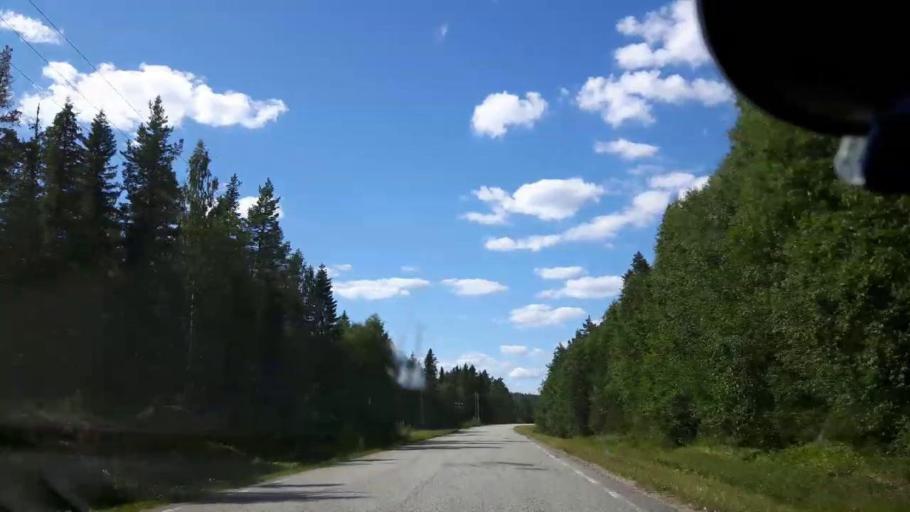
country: SE
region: Vaesternorrland
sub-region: Ange Kommun
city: Fransta
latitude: 62.7642
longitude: 16.2562
